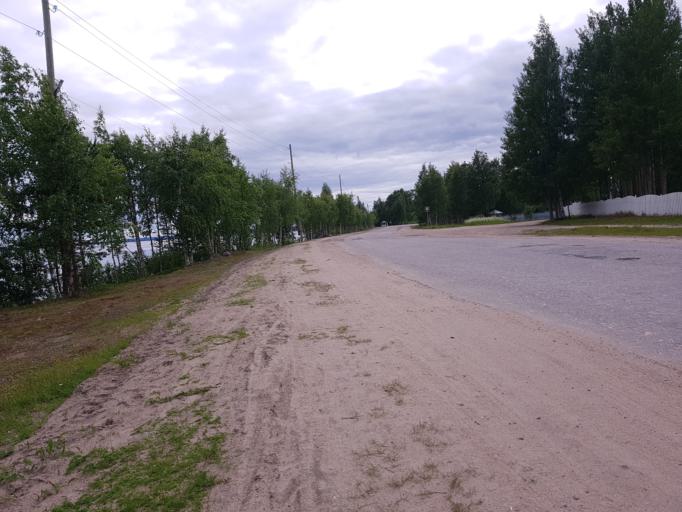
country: RU
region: Republic of Karelia
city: Kalevala
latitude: 65.1946
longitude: 31.1824
